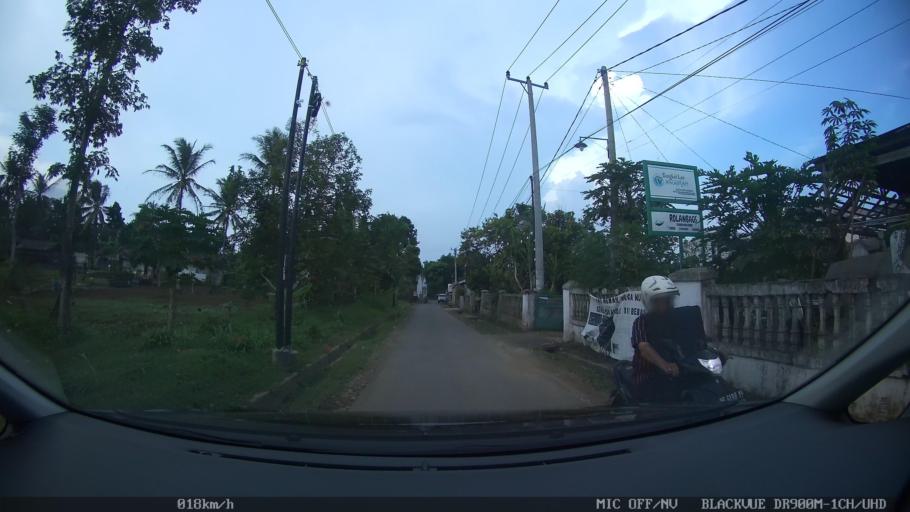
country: ID
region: Lampung
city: Kedaton
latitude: -5.3933
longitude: 105.2042
